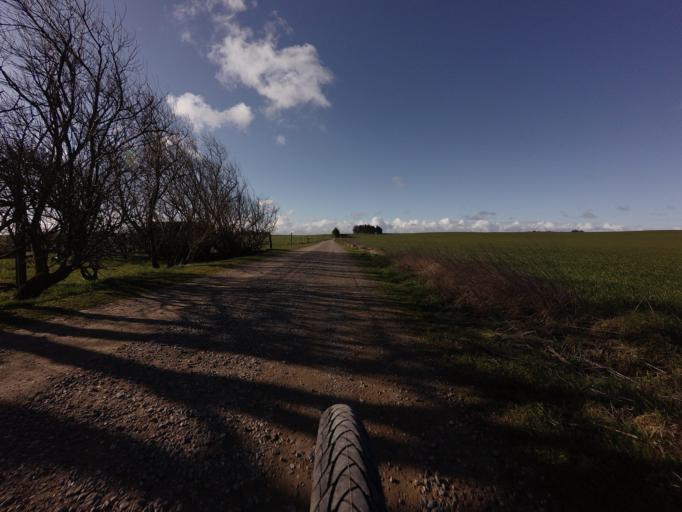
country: DK
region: North Denmark
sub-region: Hjorring Kommune
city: Vra
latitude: 57.3697
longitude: 9.8143
